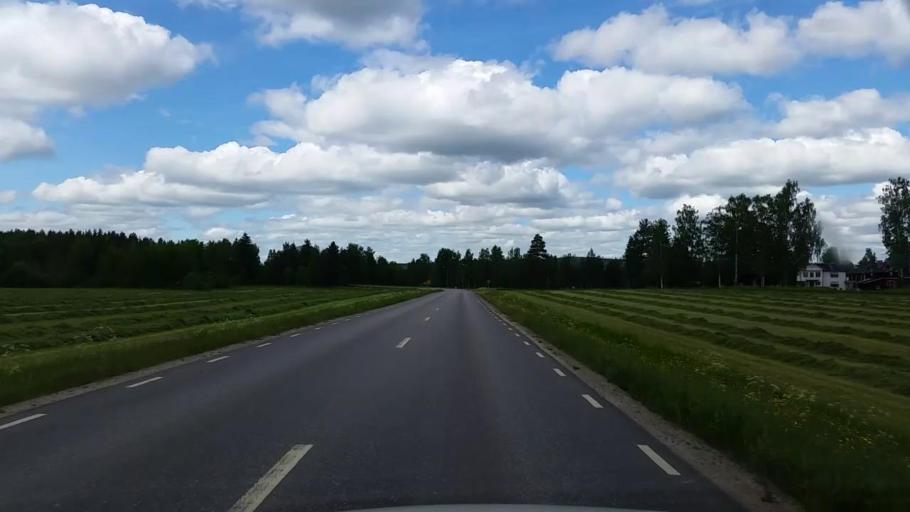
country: SE
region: Gaevleborg
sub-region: Ovanakers Kommun
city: Alfta
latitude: 61.3874
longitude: 16.0486
